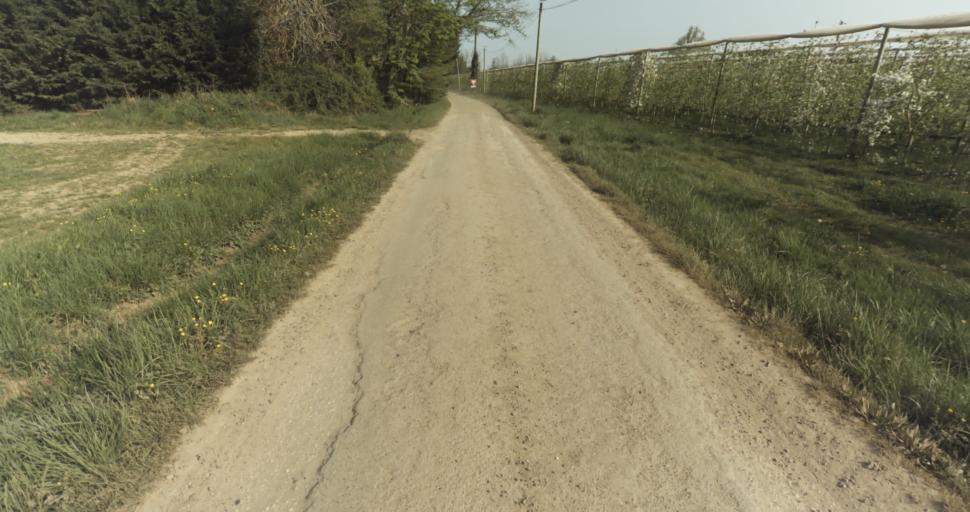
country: FR
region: Midi-Pyrenees
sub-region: Departement du Tarn-et-Garonne
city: Moissac
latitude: 44.1022
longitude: 1.1191
